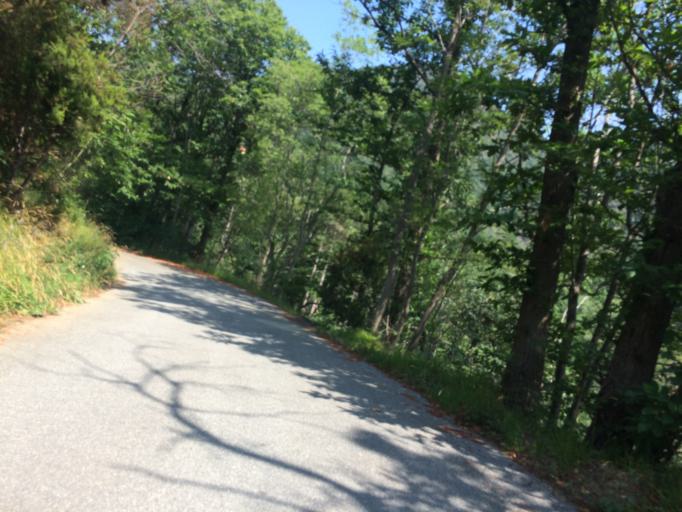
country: IT
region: Liguria
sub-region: Provincia di Genova
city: Sciarborasca
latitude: 44.4025
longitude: 8.5752
